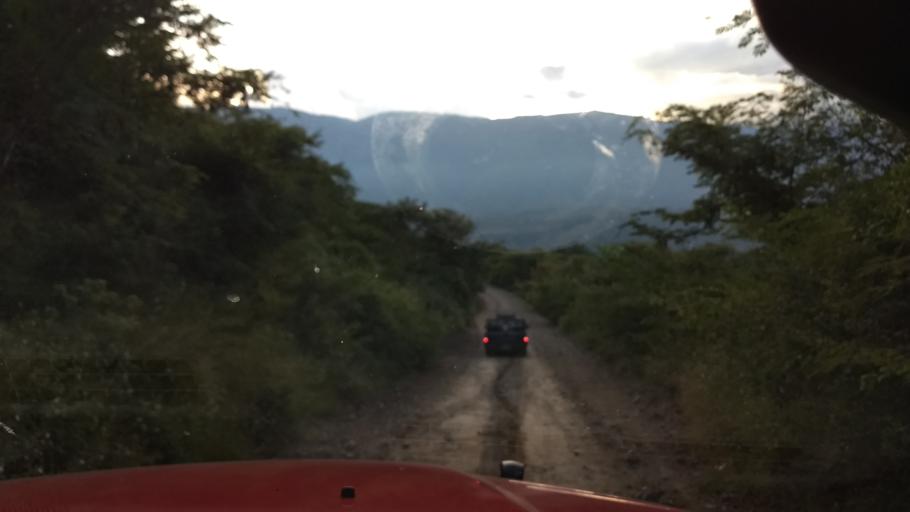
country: MX
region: Colima
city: Suchitlan
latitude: 19.4798
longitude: -103.8010
